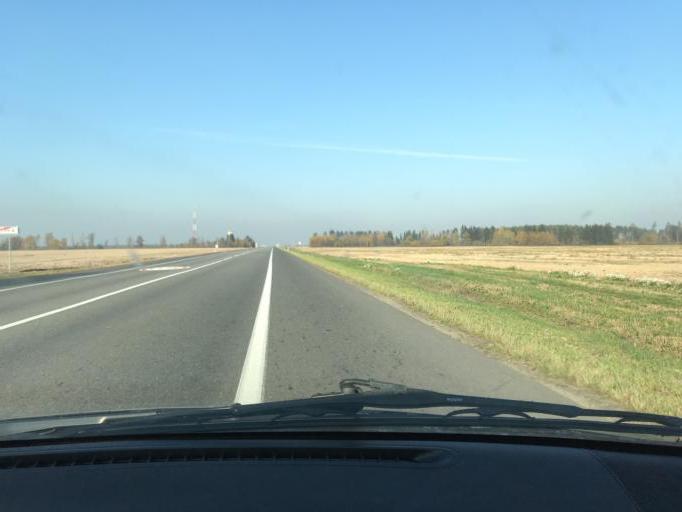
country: BY
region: Vitebsk
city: Orsha
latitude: 54.3404
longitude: 30.4461
